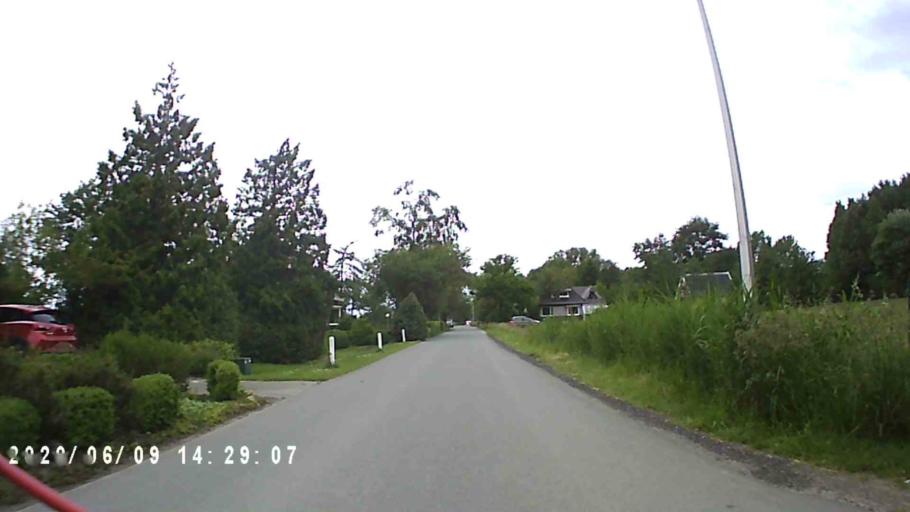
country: NL
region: Groningen
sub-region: Gemeente Bedum
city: Bedum
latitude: 53.3081
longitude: 6.5946
